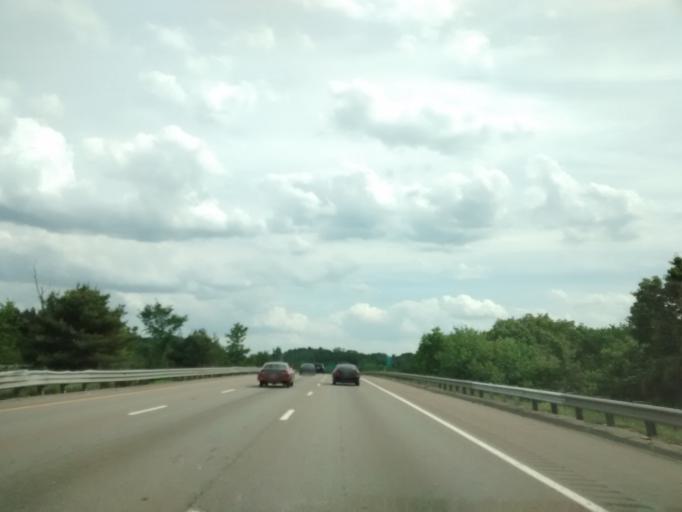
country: US
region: Massachusetts
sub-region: Worcester County
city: Cordaville
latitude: 42.2684
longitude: -71.5649
